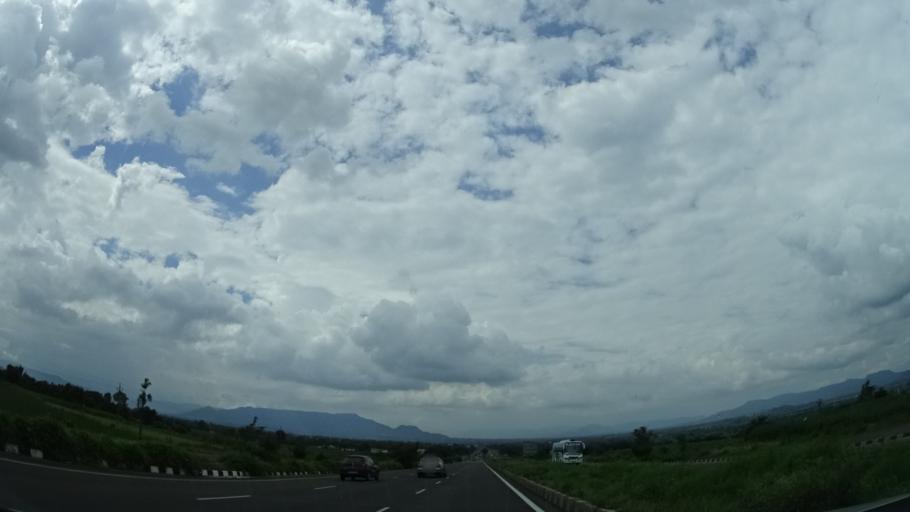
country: IN
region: Maharashtra
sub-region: Satara Division
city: Satara
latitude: 17.7922
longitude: 73.9793
